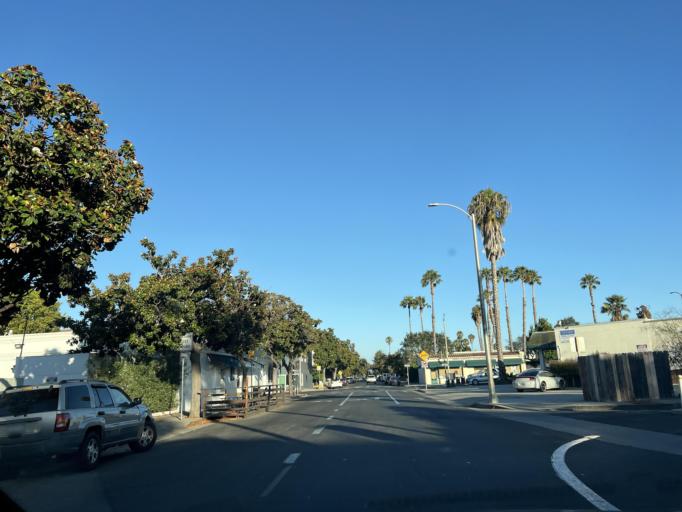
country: US
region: California
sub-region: Santa Barbara County
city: Santa Barbara
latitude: 34.4183
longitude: -119.6950
